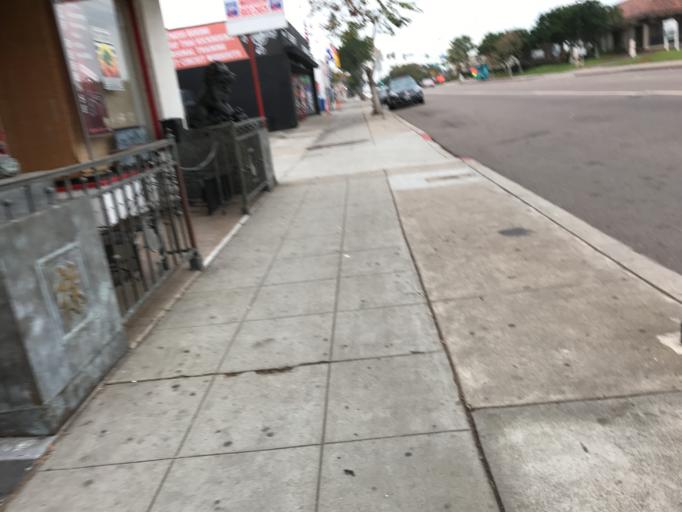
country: US
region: California
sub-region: San Diego County
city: La Jolla
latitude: 32.8004
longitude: -117.2381
